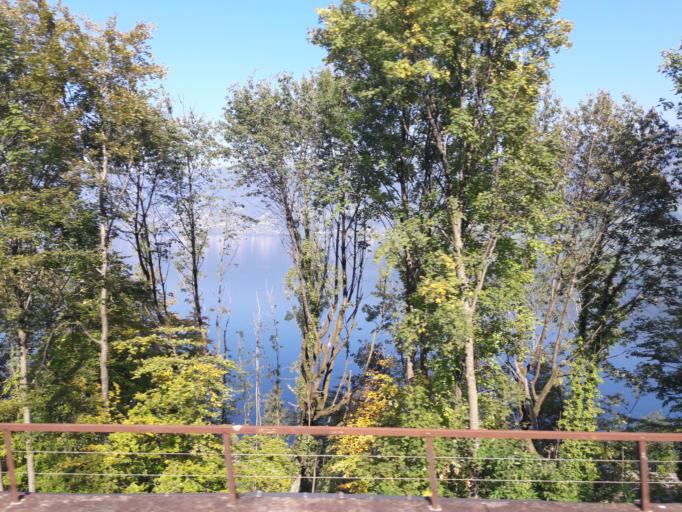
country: CH
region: Schwyz
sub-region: Bezirk Schwyz
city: Arth
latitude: 47.0709
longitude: 8.4998
